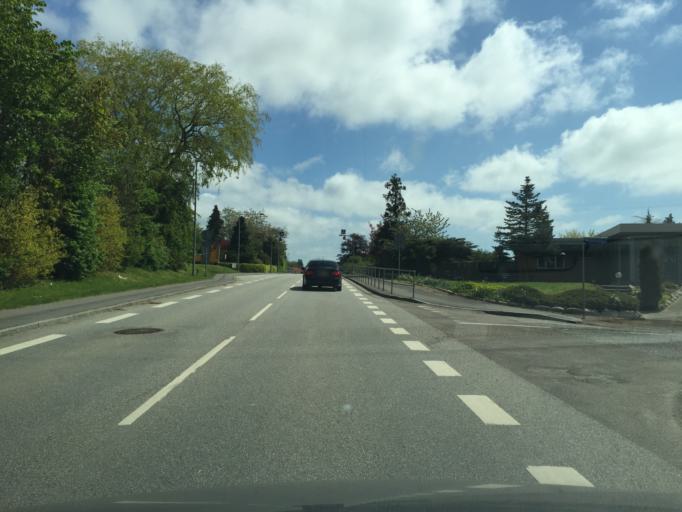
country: DK
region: Zealand
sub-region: Vordingborg Kommune
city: Nyrad
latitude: 54.9957
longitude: 12.0192
